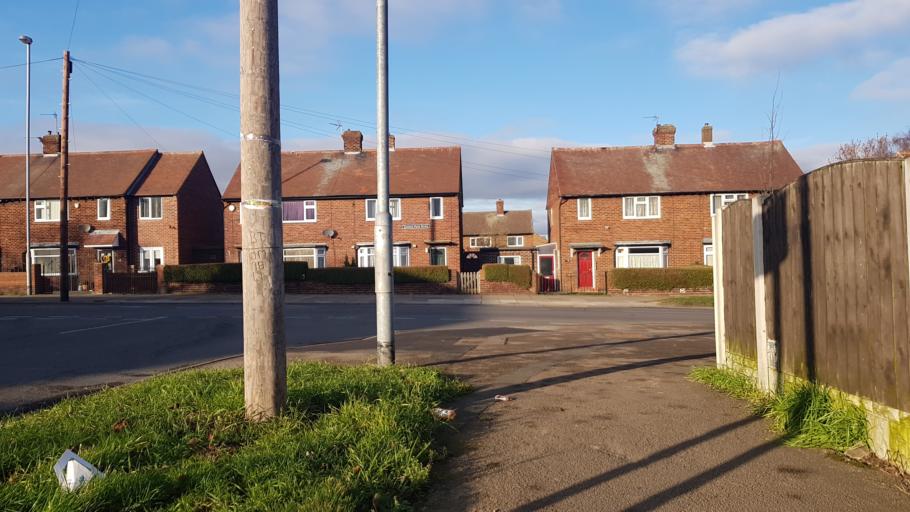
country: GB
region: England
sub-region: City and Borough of Leeds
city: Ledston
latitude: 53.7236
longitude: -1.3294
